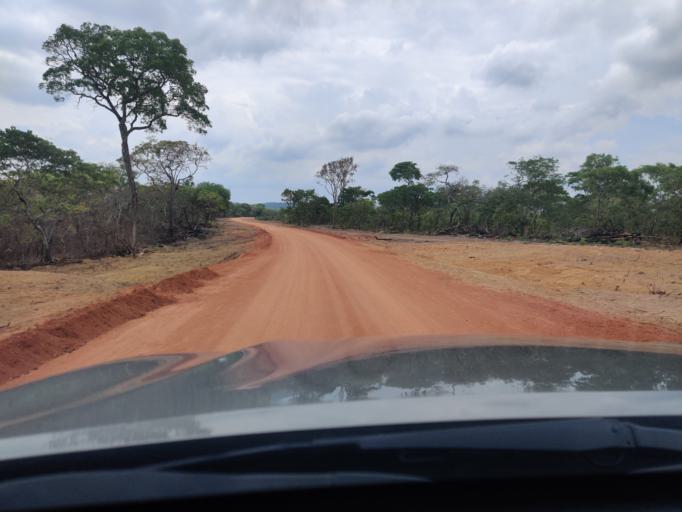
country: ZM
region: Central
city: Mkushi
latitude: -13.8074
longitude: 29.8622
